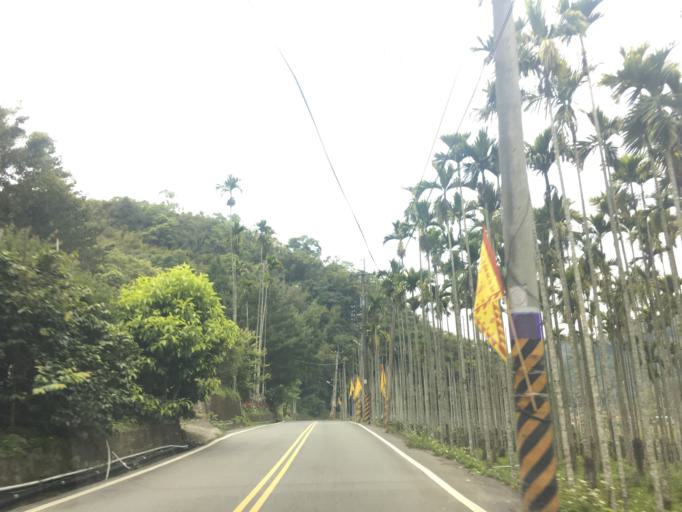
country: TW
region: Taiwan
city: Fengyuan
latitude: 24.1608
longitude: 120.8268
